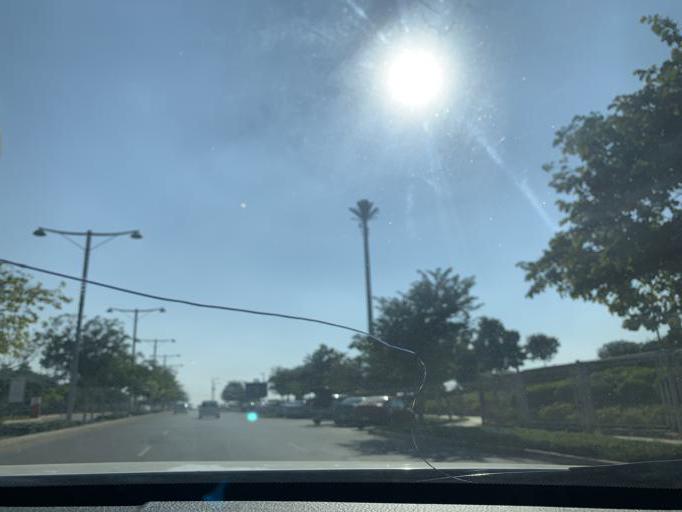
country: EG
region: Muhafazat al Qahirah
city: Cairo
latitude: 30.0331
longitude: 31.4045
